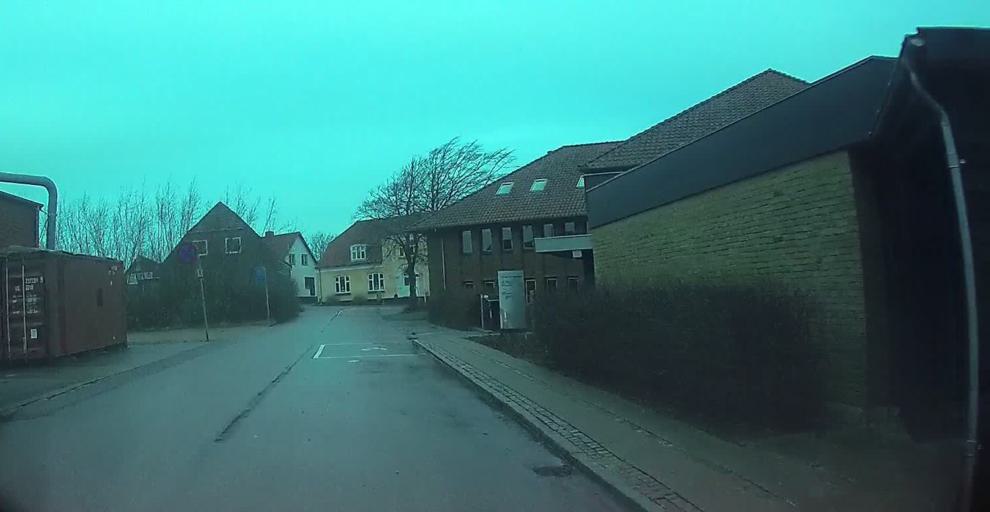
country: DK
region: North Denmark
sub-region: Thisted Kommune
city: Hurup
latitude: 56.7503
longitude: 8.4223
